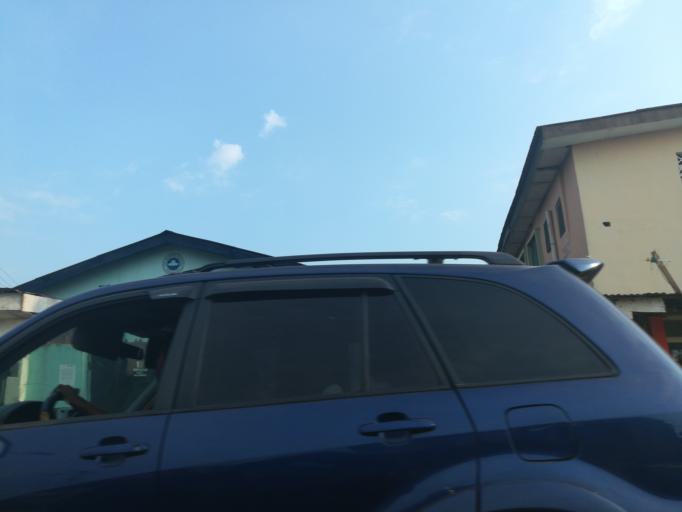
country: NG
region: Lagos
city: Ojota
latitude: 6.5875
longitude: 3.3973
